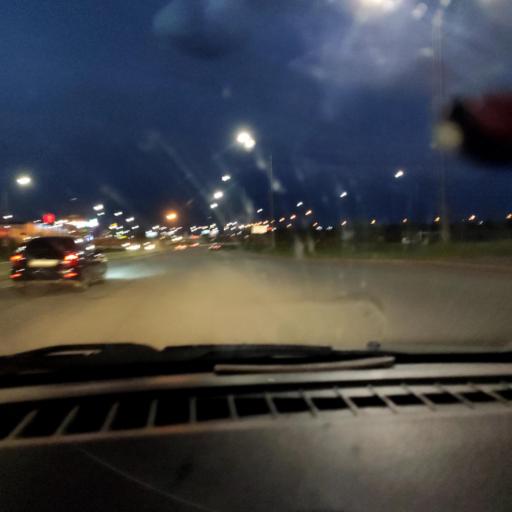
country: RU
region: Orenburg
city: Orenburg
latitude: 51.8087
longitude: 55.1765
